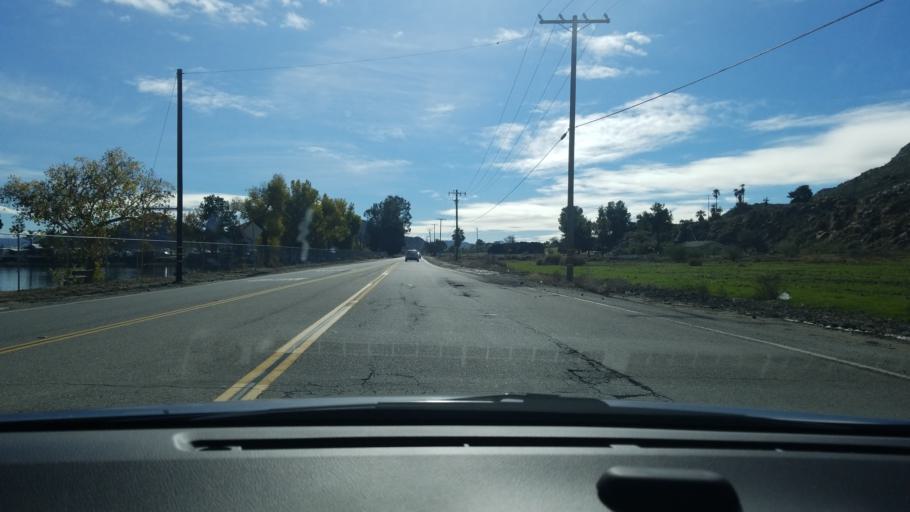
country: US
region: California
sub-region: Riverside County
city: Green Acres
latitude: 33.7863
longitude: -117.0336
